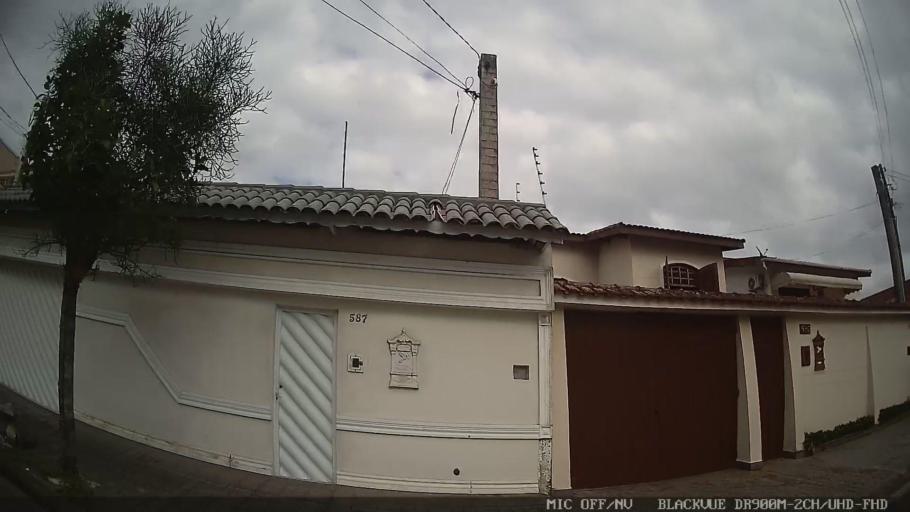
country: BR
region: Sao Paulo
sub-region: Guaruja
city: Guaruja
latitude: -23.9891
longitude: -46.2798
